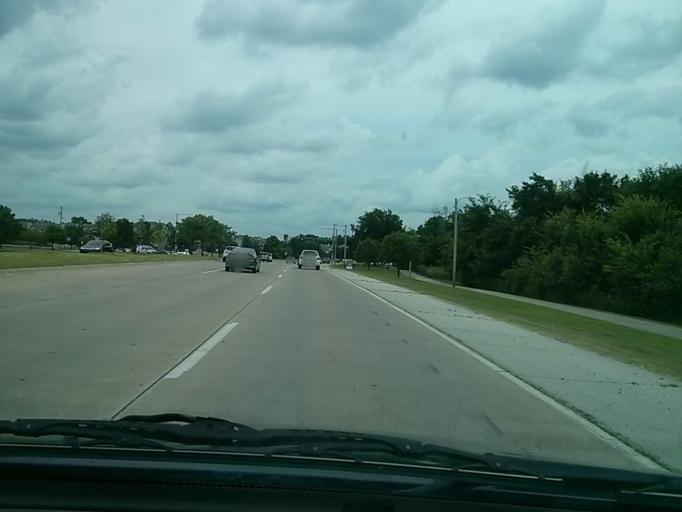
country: US
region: Oklahoma
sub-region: Tulsa County
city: Jenks
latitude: 36.0327
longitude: -95.9553
